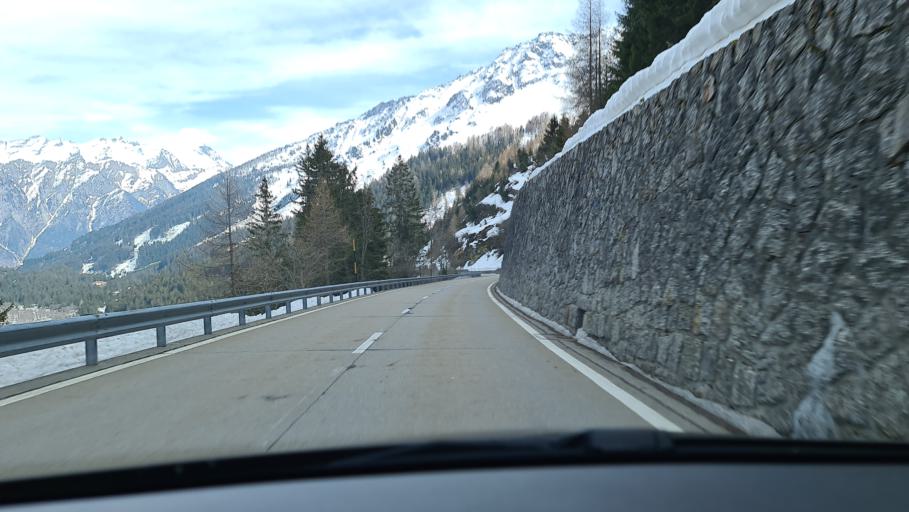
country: CH
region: Ticino
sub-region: Leventina District
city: Faido
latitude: 46.5200
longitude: 8.8585
